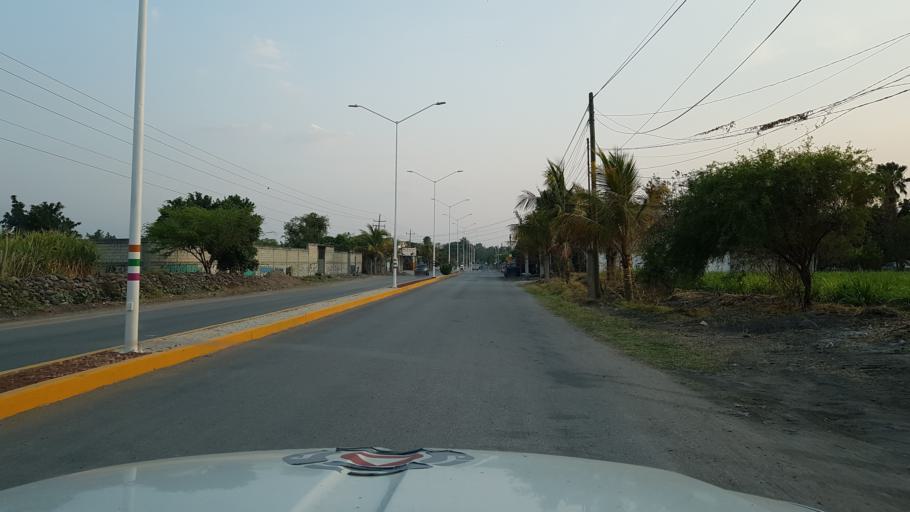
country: MX
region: Morelos
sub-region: Ayala
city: Abelardo L. Rodriguez
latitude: 18.7280
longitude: -98.9907
